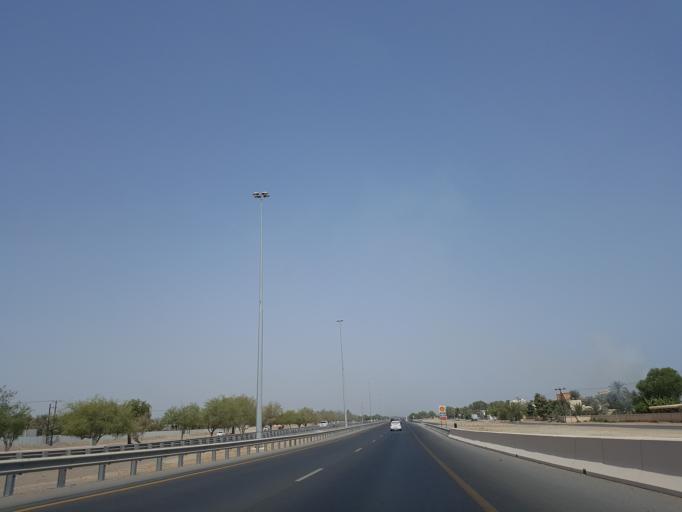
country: OM
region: Al Batinah
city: Saham
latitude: 24.0774
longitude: 56.9433
